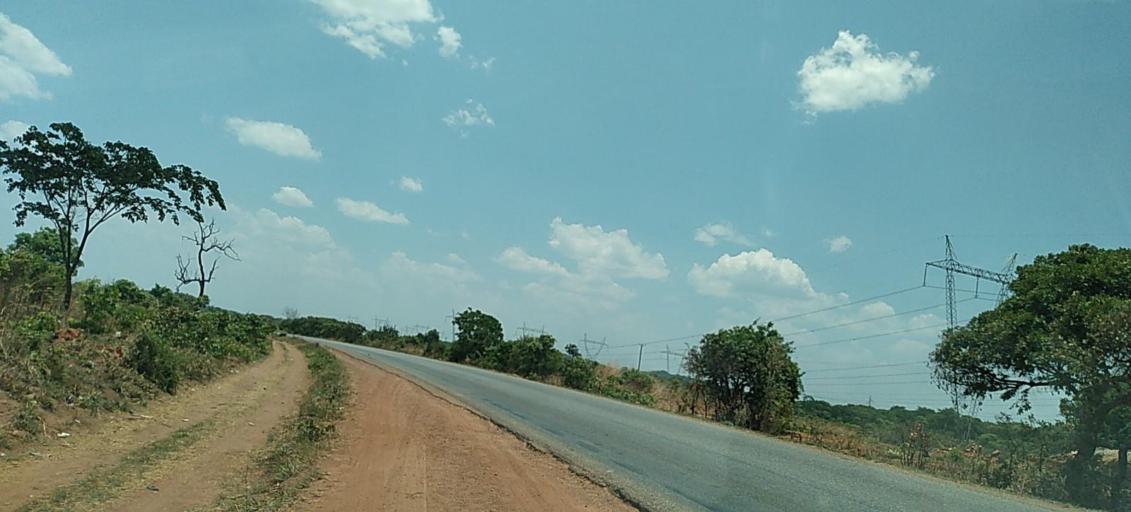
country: ZM
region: Central
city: Kapiri Mposhi
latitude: -13.6960
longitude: 28.6279
